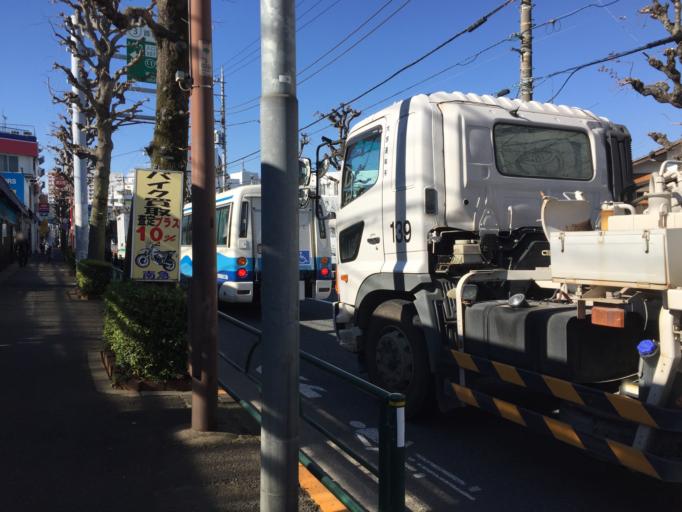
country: JP
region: Tokyo
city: Chofugaoka
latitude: 35.6376
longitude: 139.6228
